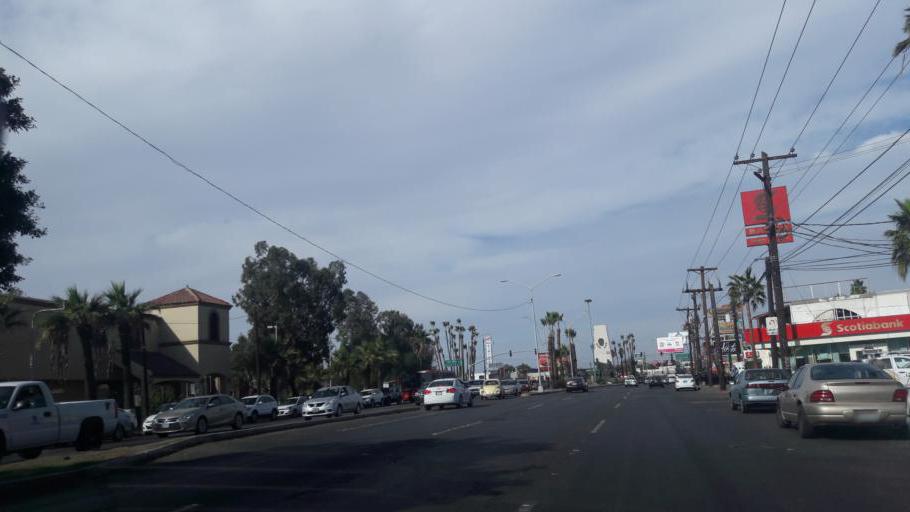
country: MX
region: Baja California
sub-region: Mexicali
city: Mexicali
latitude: 32.6458
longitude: -115.4515
